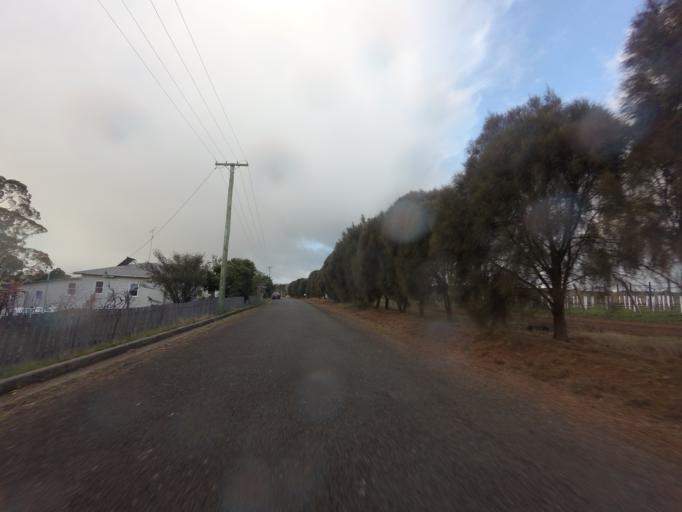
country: AU
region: Tasmania
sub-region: Break O'Day
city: St Helens
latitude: -42.0047
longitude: 148.0824
